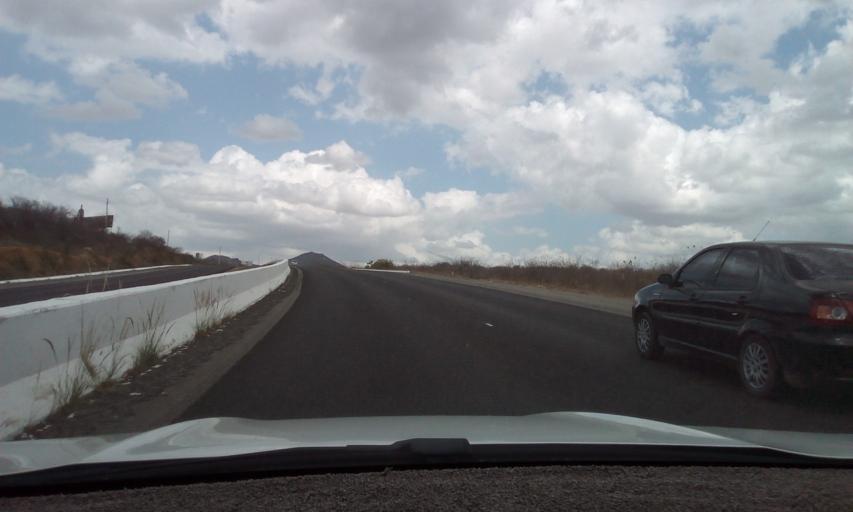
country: BR
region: Pernambuco
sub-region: Toritama
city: Toritama
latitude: -8.1143
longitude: -36.0134
